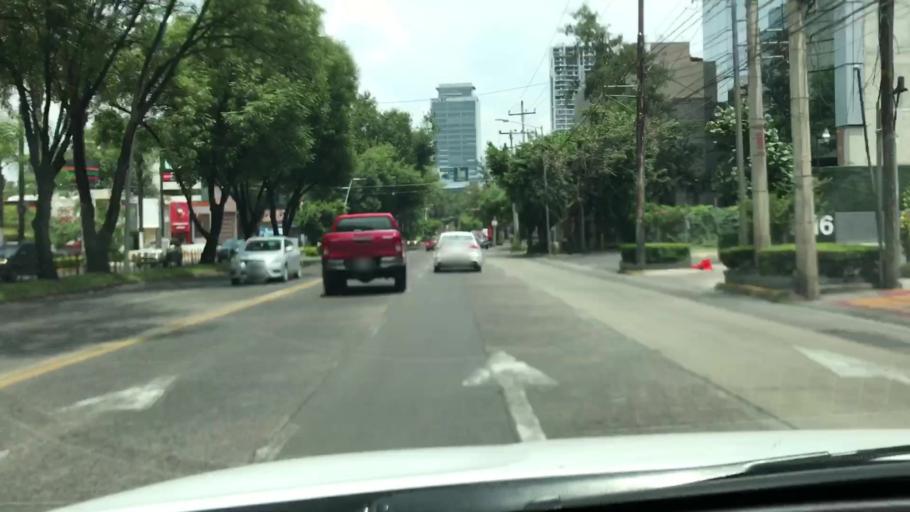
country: MX
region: Jalisco
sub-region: Zapopan
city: Zapopan
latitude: 20.7036
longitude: -103.3763
